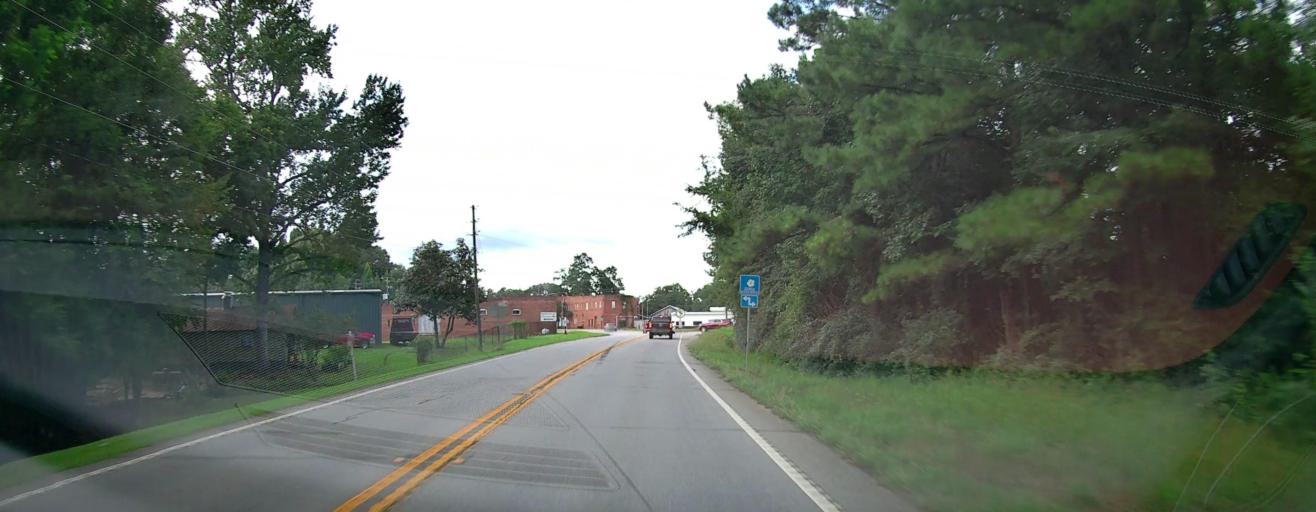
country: US
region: Georgia
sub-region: Meriwether County
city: Greenville
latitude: 33.0916
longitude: -84.5735
